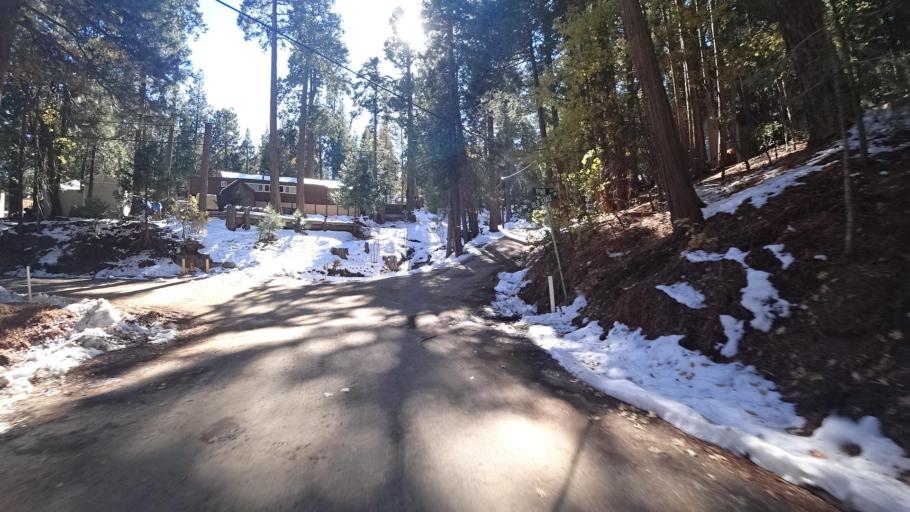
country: US
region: California
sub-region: Kern County
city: Alta Sierra
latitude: 35.7285
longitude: -118.5519
